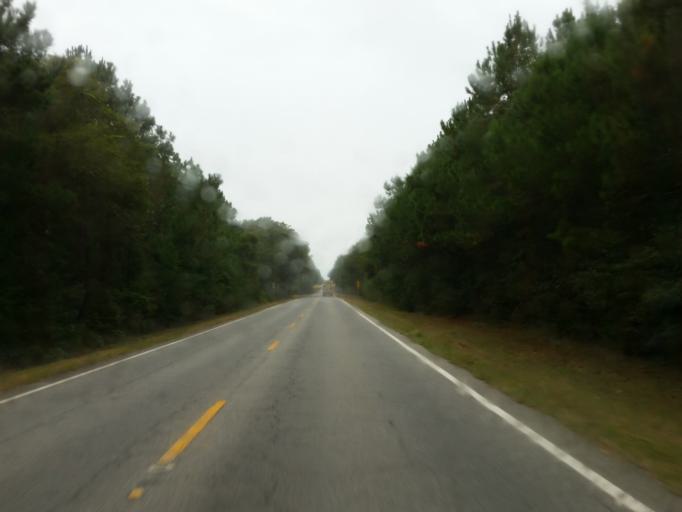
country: US
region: Georgia
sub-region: Berrien County
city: Ray City
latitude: 31.1040
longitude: -83.2798
